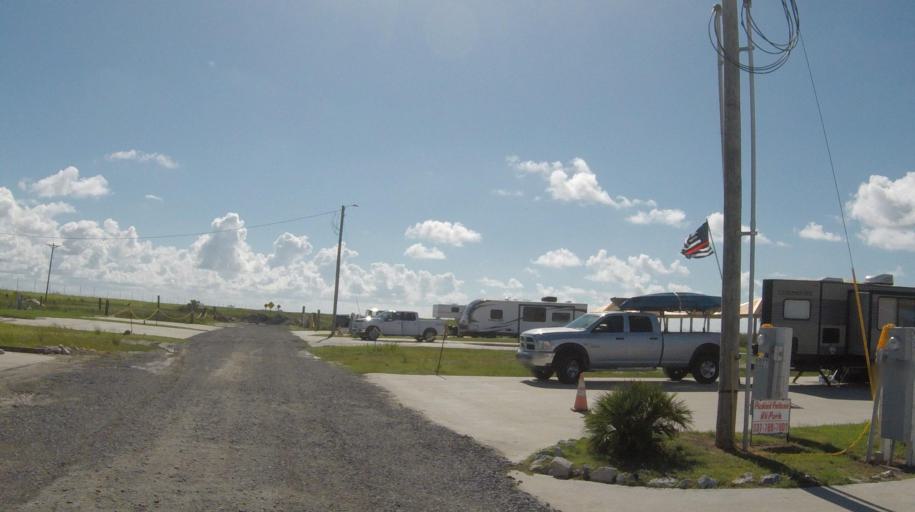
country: US
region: Louisiana
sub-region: Cameron Parish
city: Cameron
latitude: 29.7699
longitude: -93.4464
